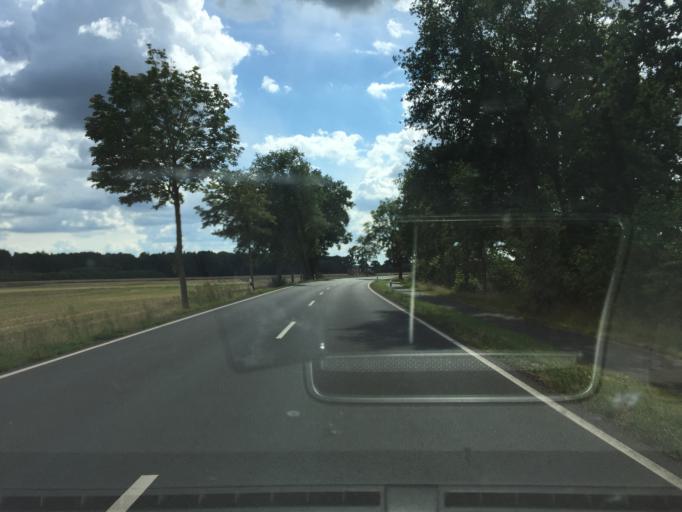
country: DE
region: Lower Saxony
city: Heemsen
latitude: 52.7295
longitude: 9.2927
